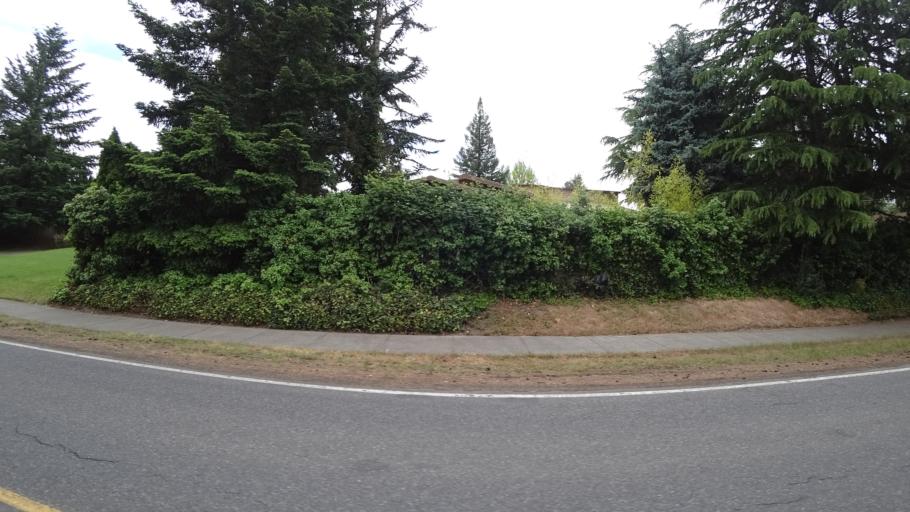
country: US
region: Oregon
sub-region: Washington County
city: Garden Home-Whitford
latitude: 45.4658
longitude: -122.7567
